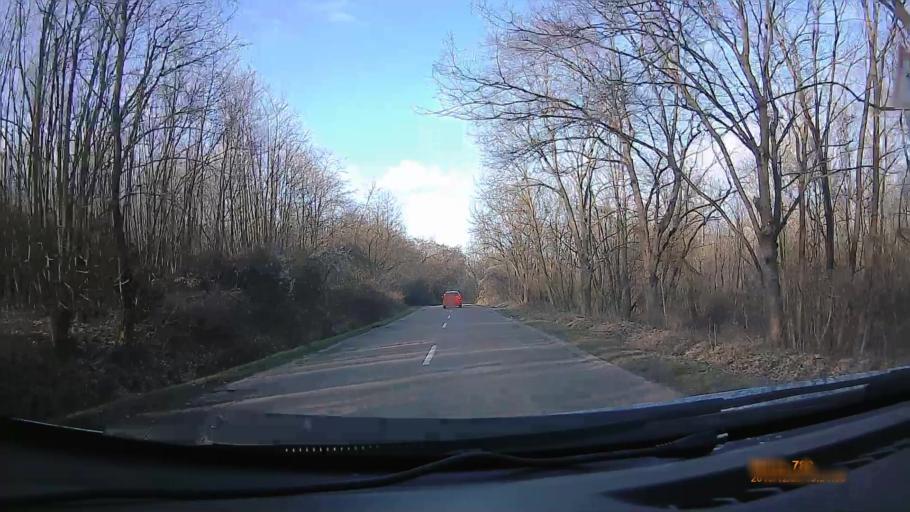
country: HU
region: Heves
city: Verpelet
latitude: 47.8799
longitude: 20.1958
